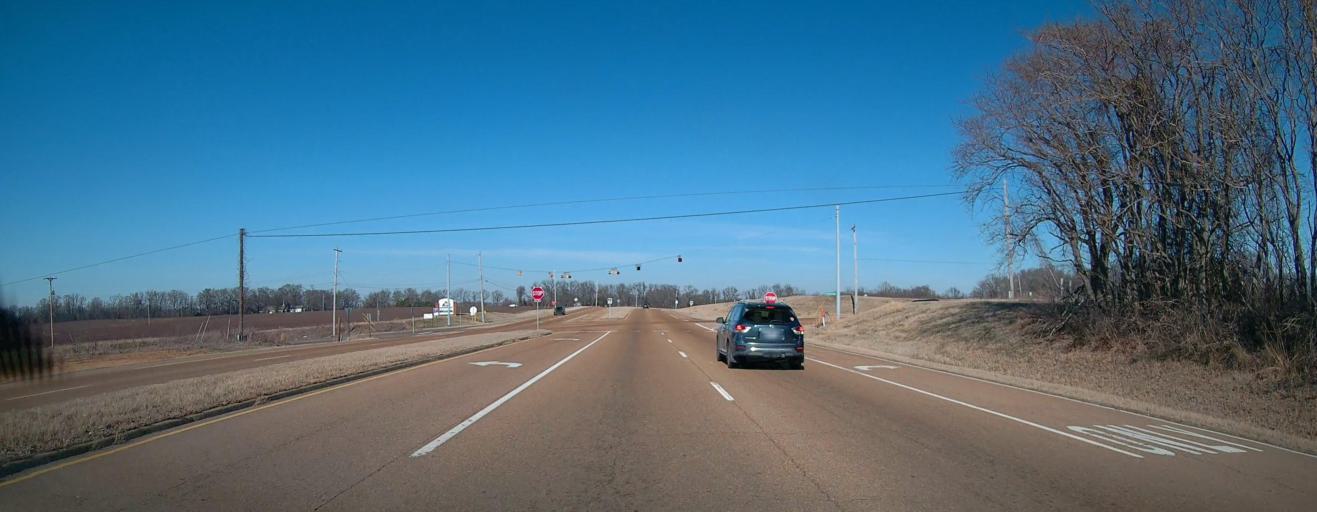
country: US
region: Tennessee
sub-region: Shelby County
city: Millington
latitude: 35.3052
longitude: -89.8817
